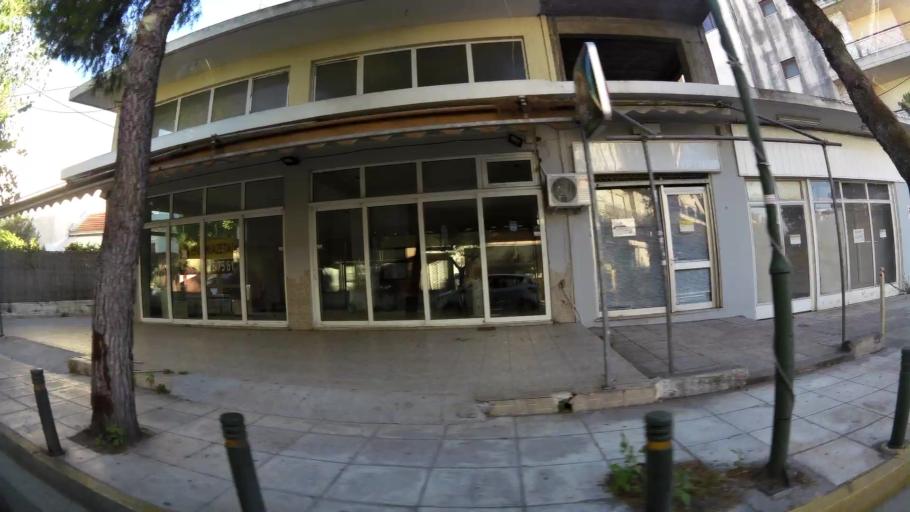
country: GR
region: Attica
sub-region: Nomarchia Athinas
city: Lykovrysi
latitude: 38.0600
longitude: 23.7762
